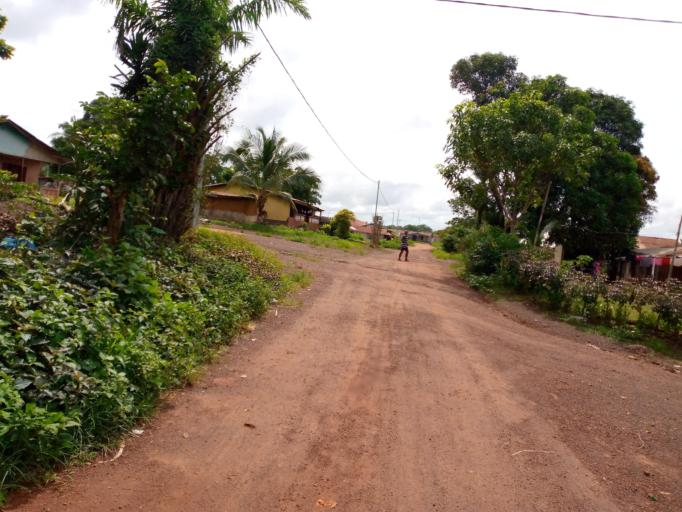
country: SL
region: Southern Province
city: Mogbwemo
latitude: 7.7592
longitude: -12.3077
